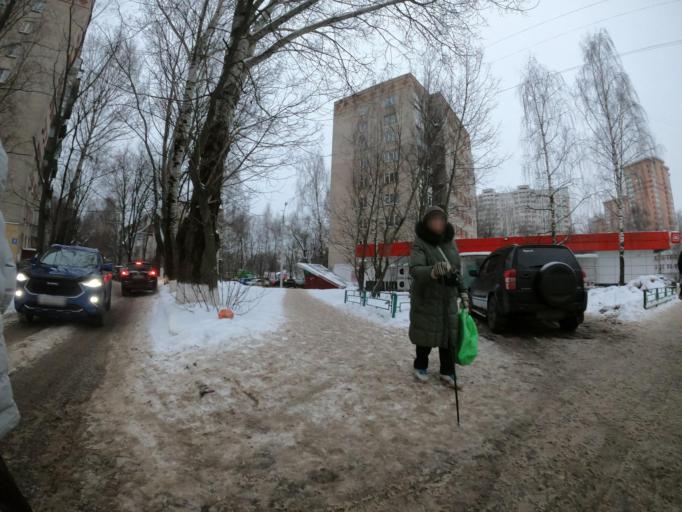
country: RU
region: Moskovskaya
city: Dubrovitsy
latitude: 55.4258
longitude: 37.5009
